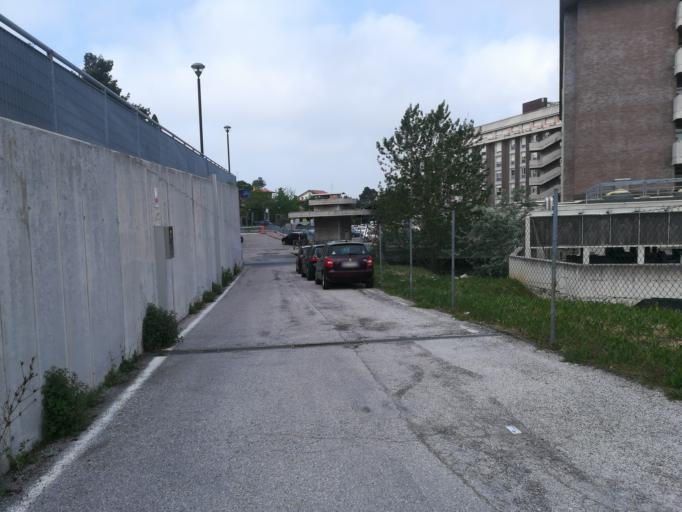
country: IT
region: The Marches
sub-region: Provincia di Macerata
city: Macerata
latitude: 43.2944
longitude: 13.4606
